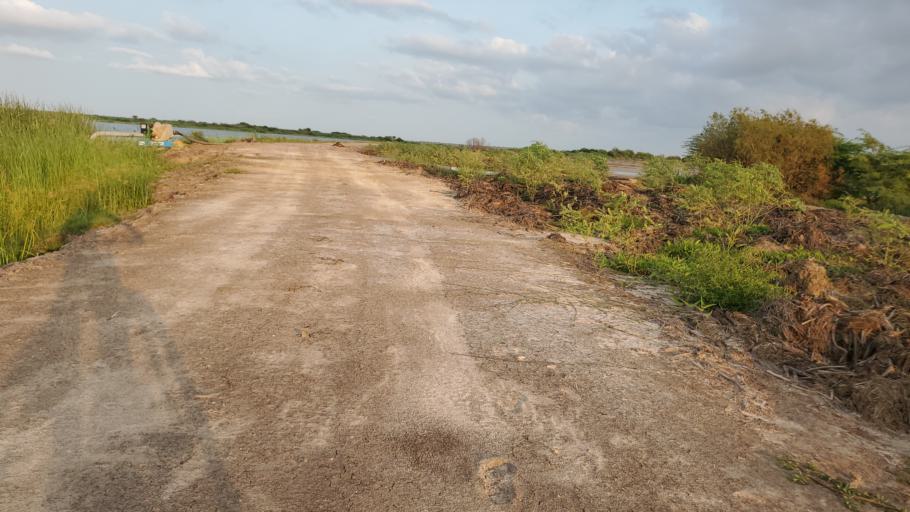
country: SN
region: Saint-Louis
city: Saint-Louis
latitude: 16.0188
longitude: -16.4047
